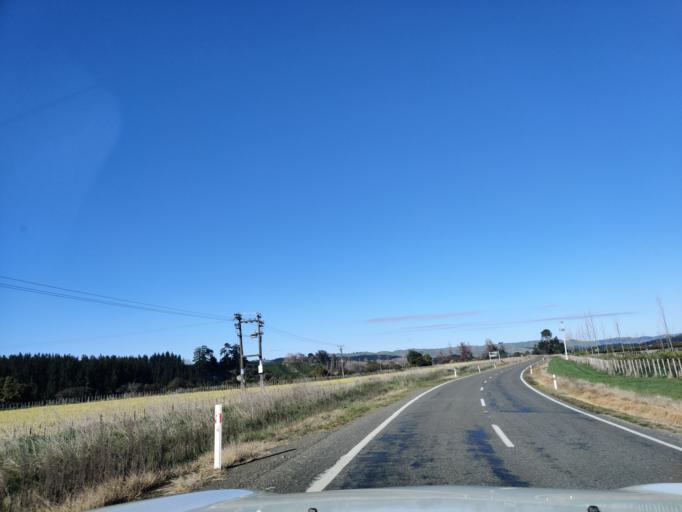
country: NZ
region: Manawatu-Wanganui
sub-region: Rangitikei District
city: Bulls
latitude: -39.9438
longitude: 175.6491
